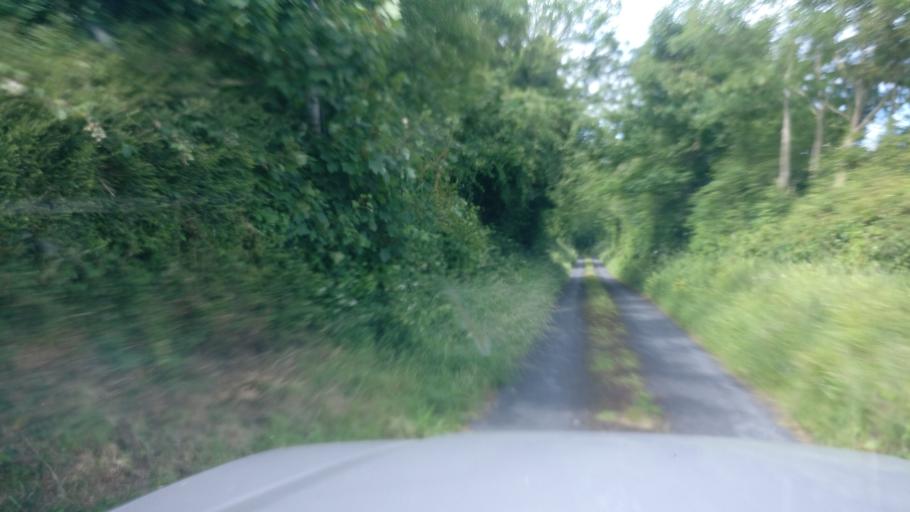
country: IE
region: Connaught
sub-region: County Galway
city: Gort
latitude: 53.0784
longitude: -8.7720
